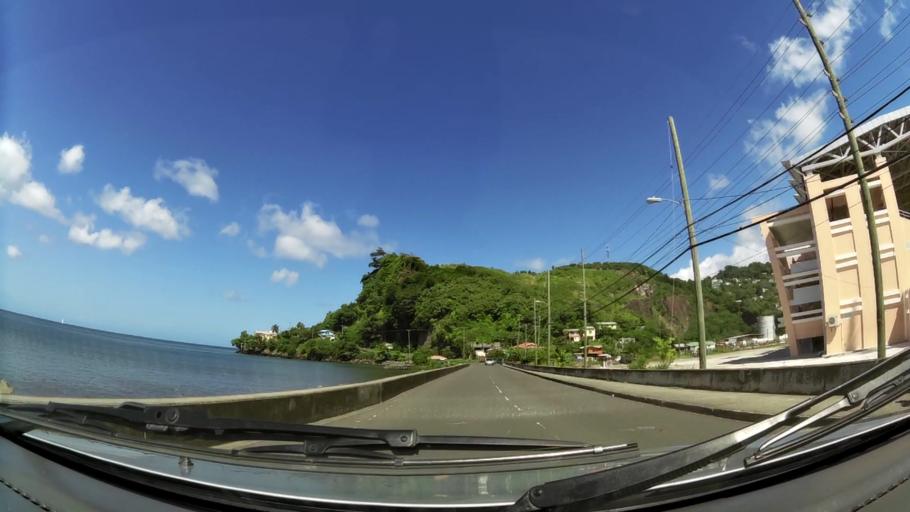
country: GD
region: Saint George
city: Saint George's
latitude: 12.0598
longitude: -61.7547
